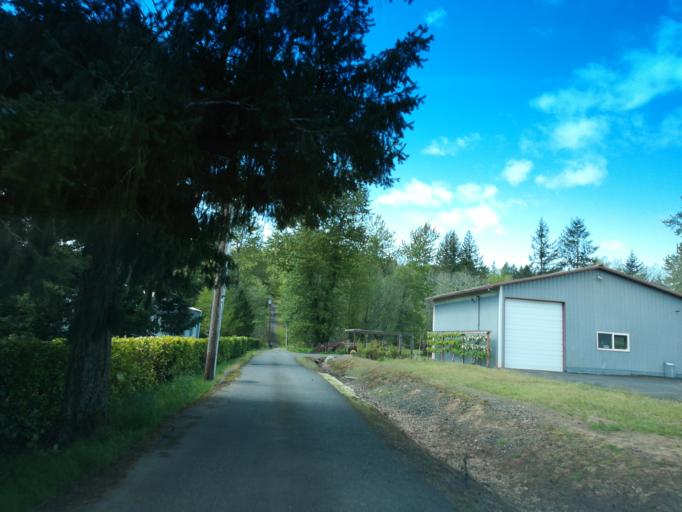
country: US
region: Oregon
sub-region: Clackamas County
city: Damascus
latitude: 45.4450
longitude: -122.4356
